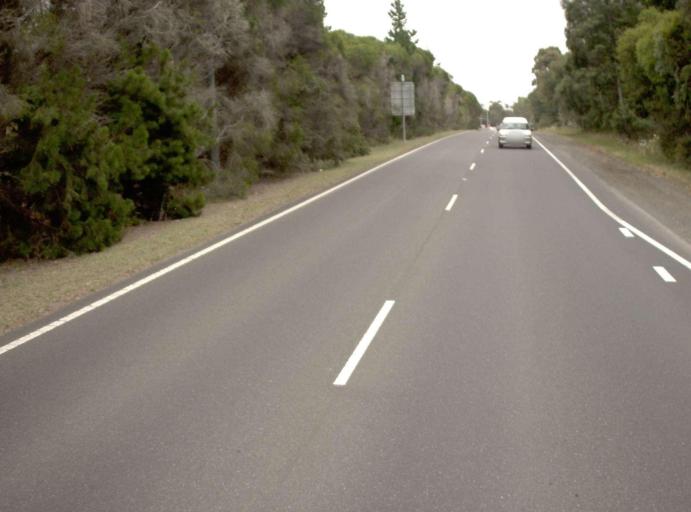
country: AU
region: Victoria
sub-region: Cardinia
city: Pakenham Upper
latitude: -38.0687
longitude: 145.4959
